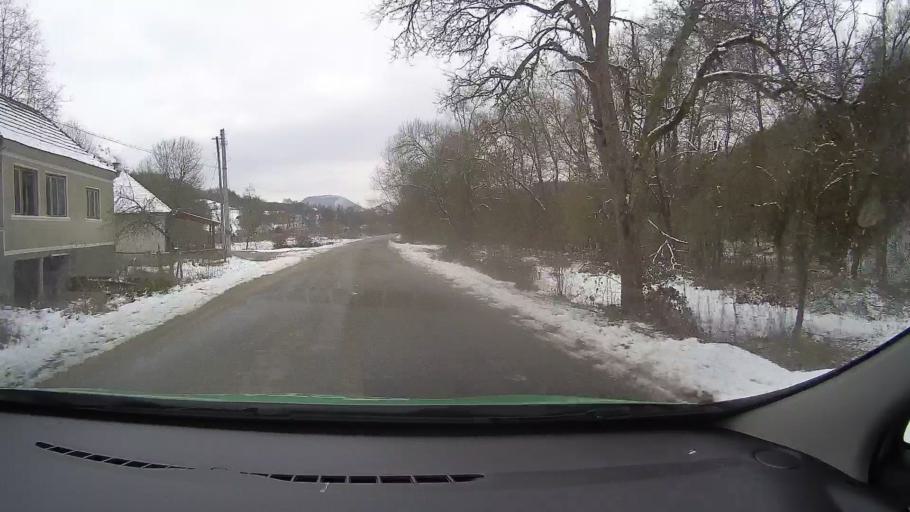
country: RO
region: Hunedoara
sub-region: Comuna Balsa
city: Balsa
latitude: 46.0422
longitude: 23.0716
